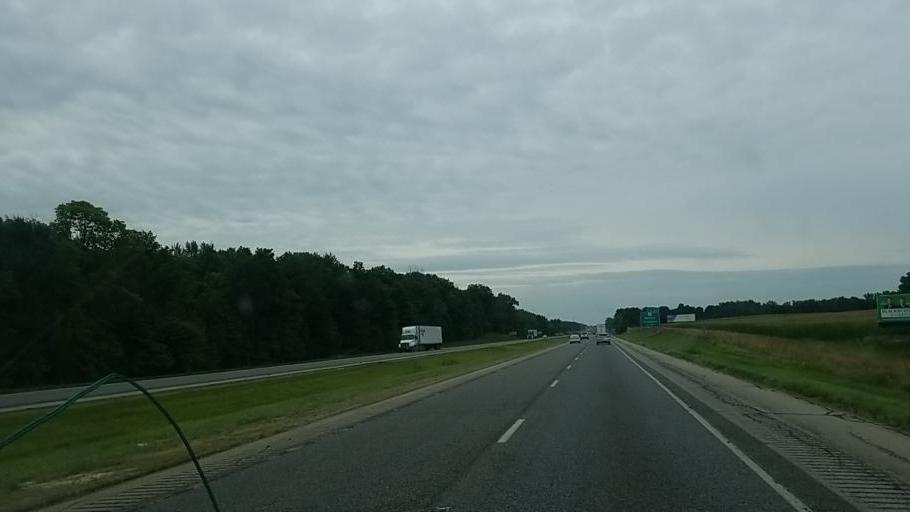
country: US
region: Indiana
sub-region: DeKalb County
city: Waterloo
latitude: 41.4533
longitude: -85.0541
